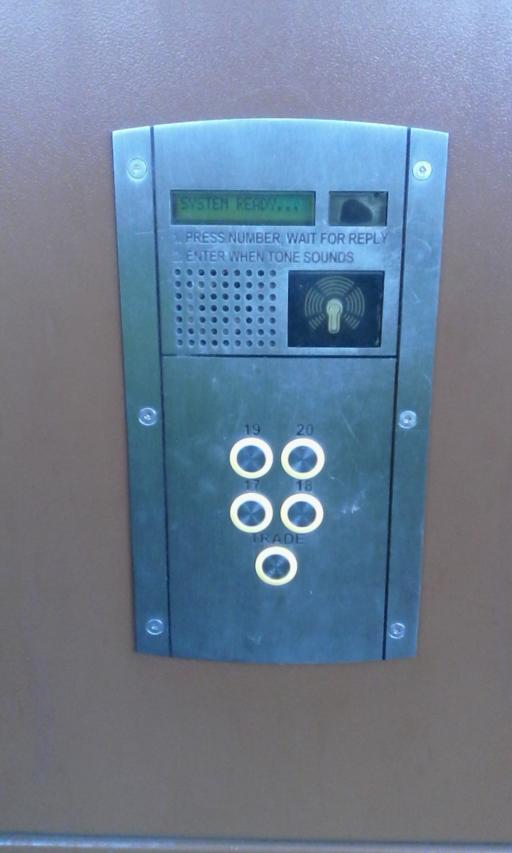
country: GB
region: England
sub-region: Nottingham
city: Nottingham
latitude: 52.9625
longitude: -1.1241
